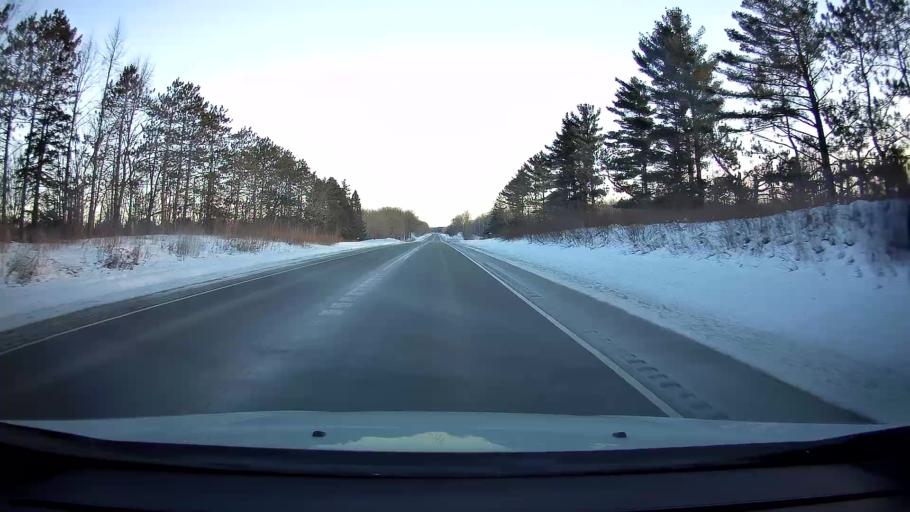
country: US
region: Wisconsin
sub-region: Washburn County
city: Shell Lake
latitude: 45.6947
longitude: -91.9650
